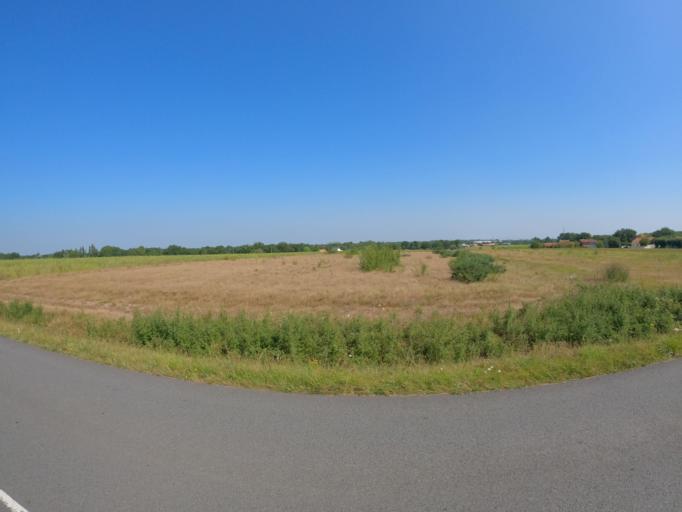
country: FR
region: Pays de la Loire
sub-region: Departement de la Loire-Atlantique
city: Pont-Saint-Martin
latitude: 47.1197
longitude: -1.5646
